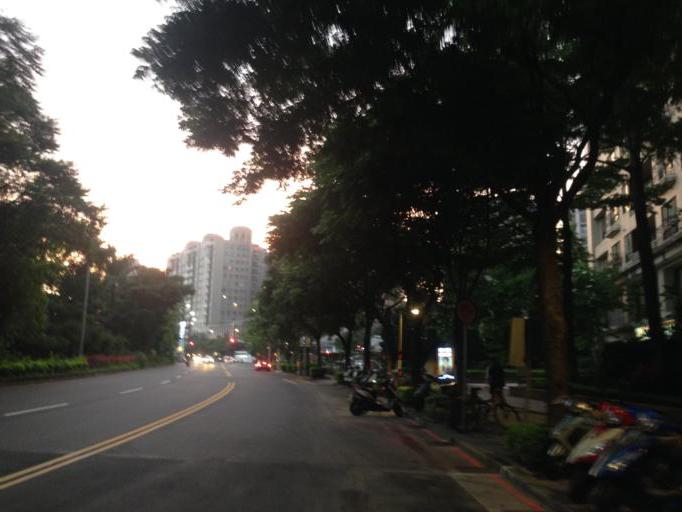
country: TW
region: Taiwan
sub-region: Taoyuan
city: Taoyuan
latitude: 24.9403
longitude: 121.3750
